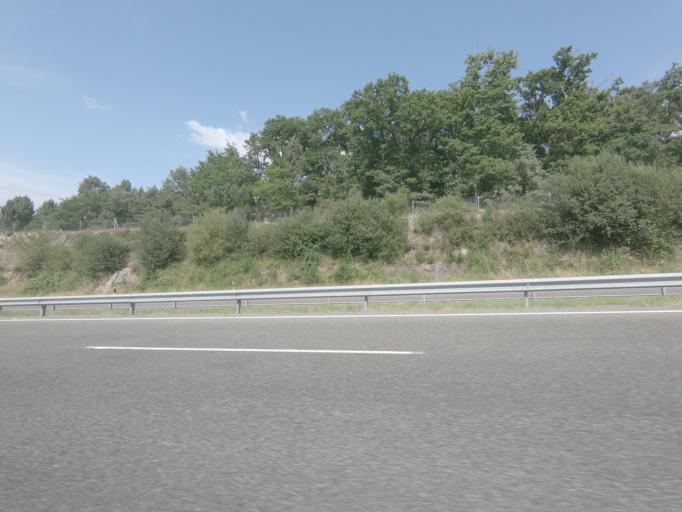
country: ES
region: Galicia
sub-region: Provincia de Ourense
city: Taboadela
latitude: 42.2728
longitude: -7.8721
